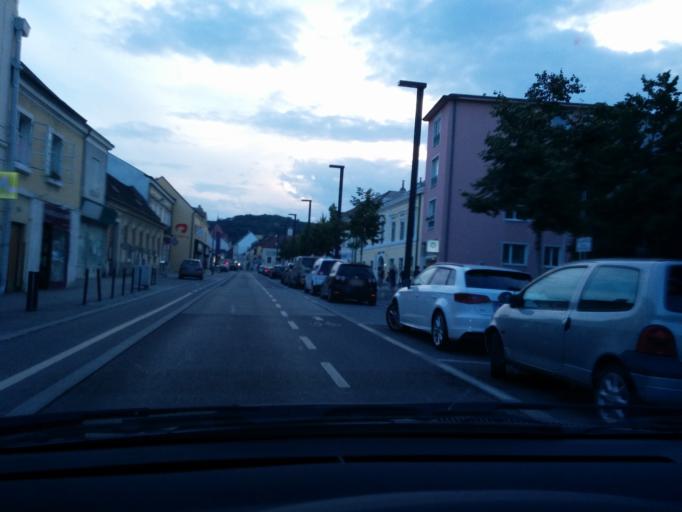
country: AT
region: Lower Austria
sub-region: Politischer Bezirk Modling
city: Modling
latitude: 48.0863
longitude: 16.2897
